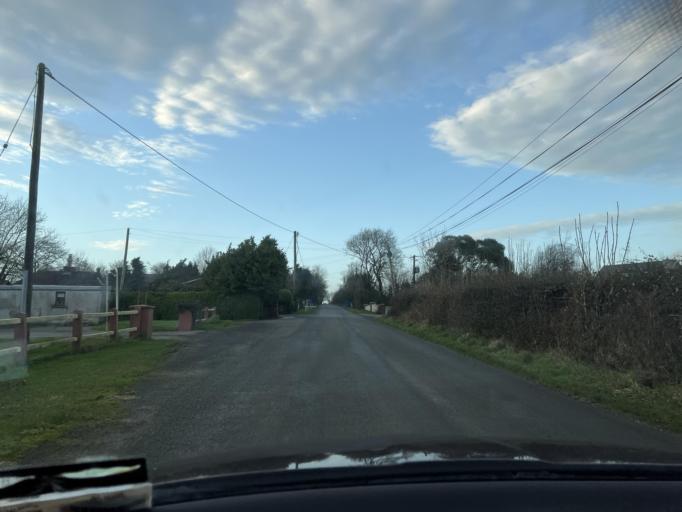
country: IE
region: Leinster
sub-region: Loch Garman
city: Loch Garman
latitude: 52.3618
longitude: -6.5227
